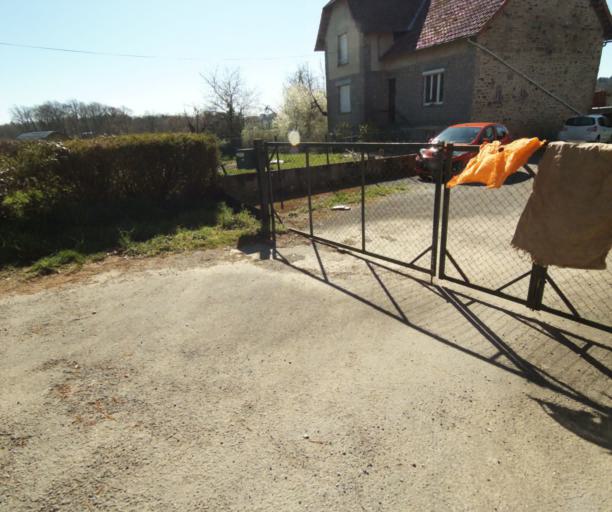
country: FR
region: Limousin
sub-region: Departement de la Correze
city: Chamboulive
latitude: 45.4311
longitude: 1.6918
